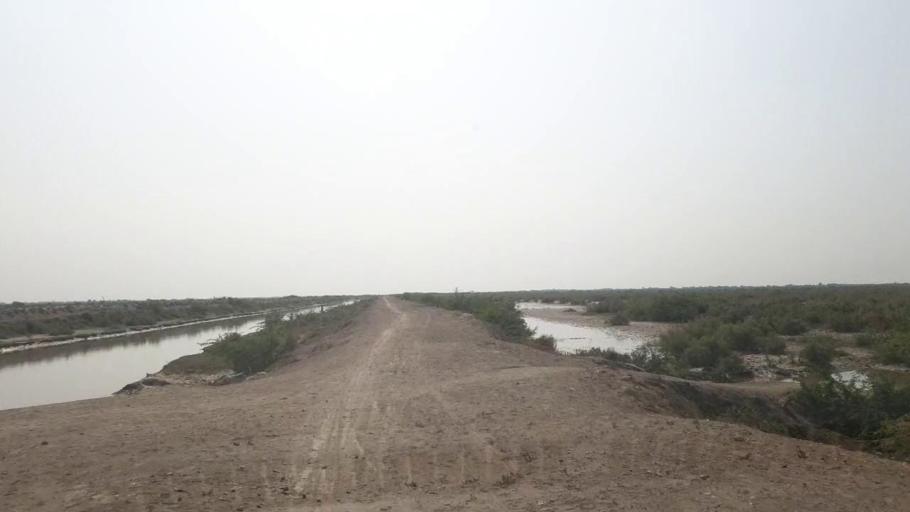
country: PK
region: Sindh
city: Kadhan
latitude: 24.3799
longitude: 68.8974
